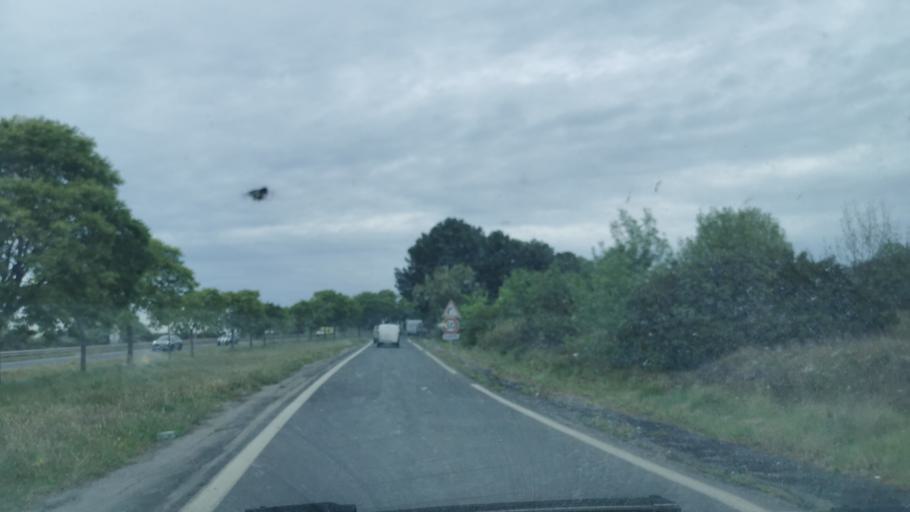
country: FR
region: Languedoc-Roussillon
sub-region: Departement de l'Herault
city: Balaruc-le-Vieux
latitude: 43.4736
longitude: 3.6850
